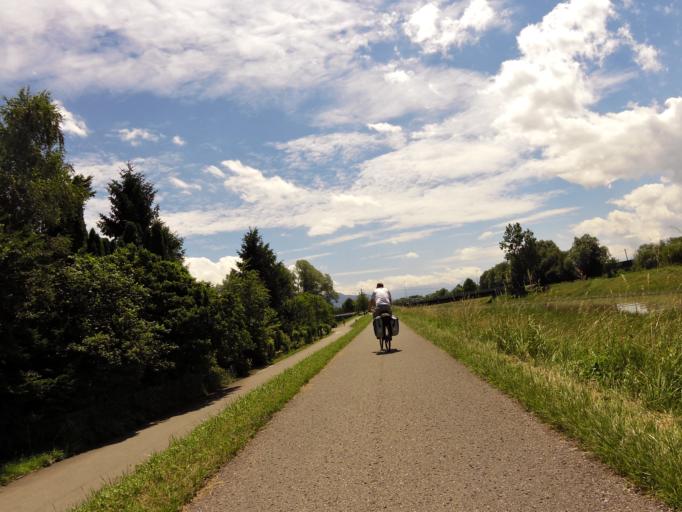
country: AT
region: Vorarlberg
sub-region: Politischer Bezirk Bregenz
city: Hard
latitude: 47.4797
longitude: 9.6750
